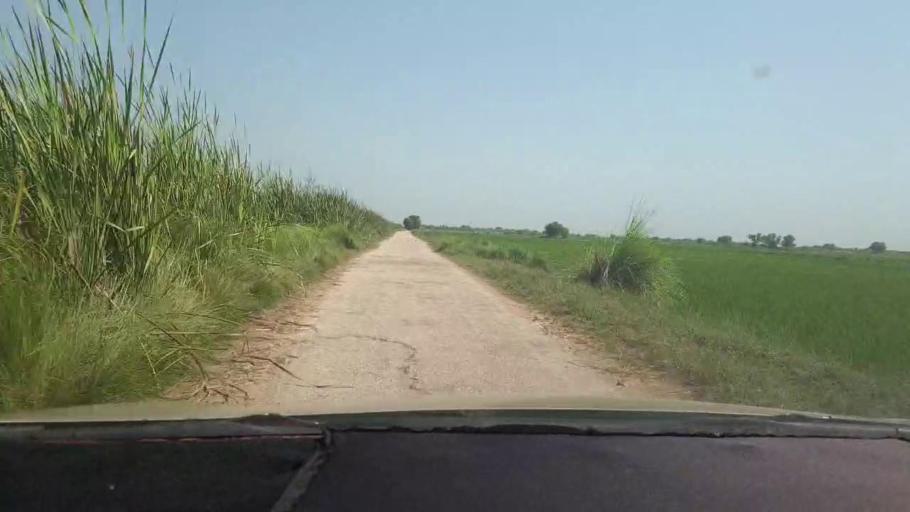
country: PK
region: Sindh
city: Miro Khan
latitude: 27.7003
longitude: 68.0915
